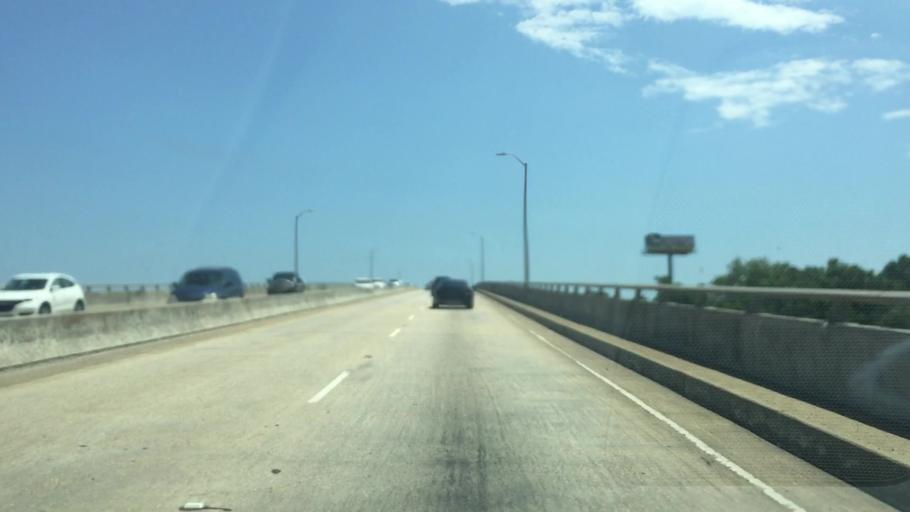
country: US
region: South Carolina
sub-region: Horry County
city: Little River
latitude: 33.8554
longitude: -78.6552
